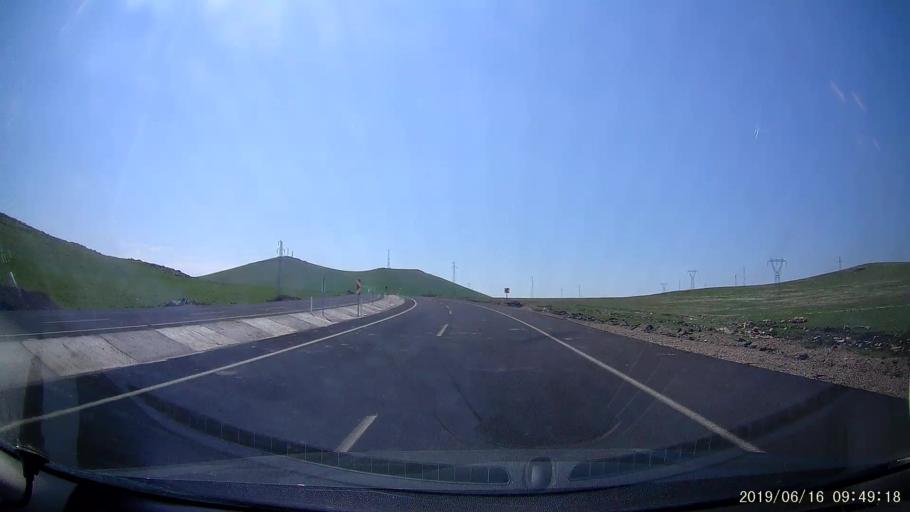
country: TR
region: Kars
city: Digor
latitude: 40.4227
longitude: 43.3575
